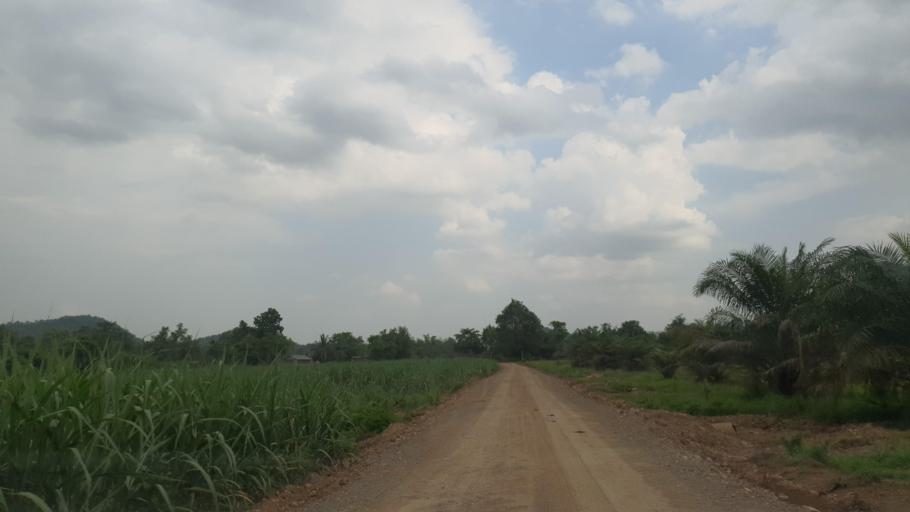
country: TH
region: Sukhothai
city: Thung Saliam
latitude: 17.2530
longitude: 99.5426
